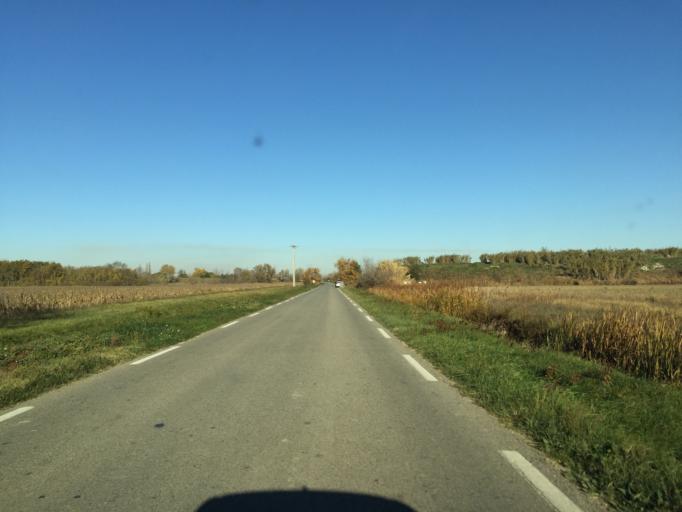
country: FR
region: Provence-Alpes-Cote d'Azur
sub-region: Departement du Vaucluse
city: Bedarrides
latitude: 44.0271
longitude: 4.9157
